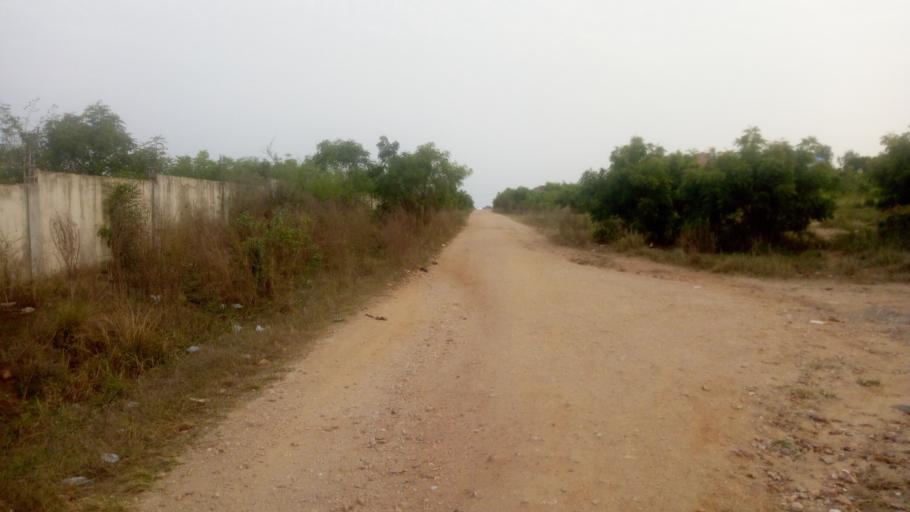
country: GH
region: Central
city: Winneba
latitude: 5.3783
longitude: -0.6288
